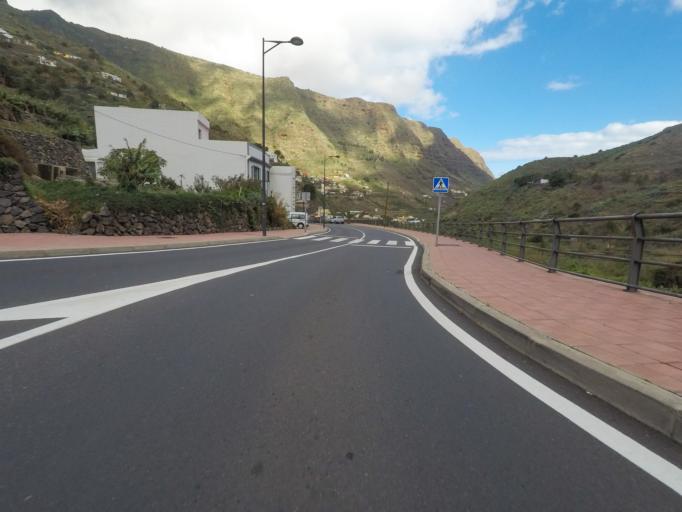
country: ES
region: Canary Islands
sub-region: Provincia de Santa Cruz de Tenerife
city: Hermigua
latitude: 28.1581
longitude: -17.1979
